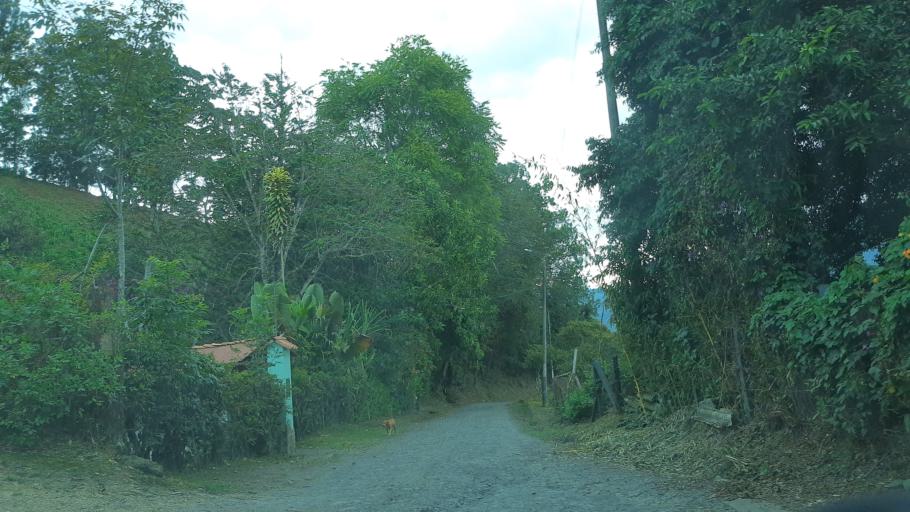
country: CO
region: Boyaca
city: Chivor
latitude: 4.9752
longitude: -73.3205
